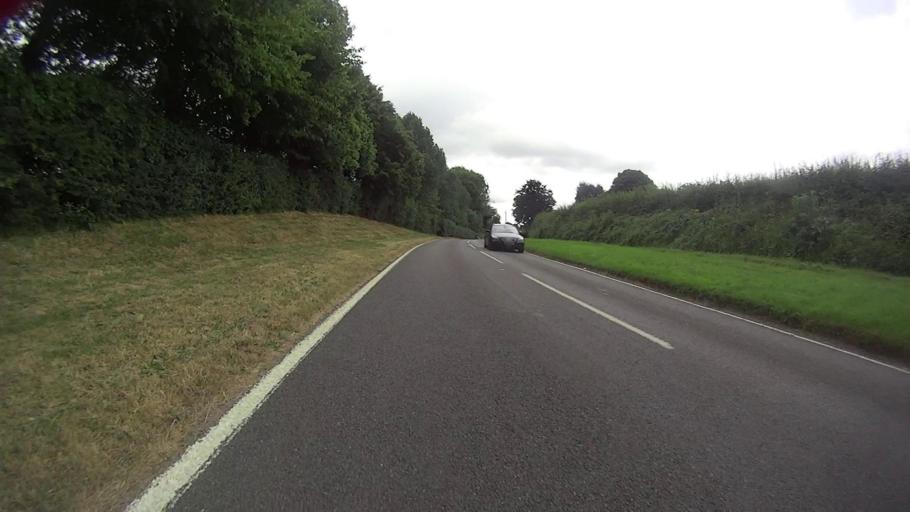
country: GB
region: England
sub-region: Surrey
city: Reigate
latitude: 51.1874
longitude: -0.2335
